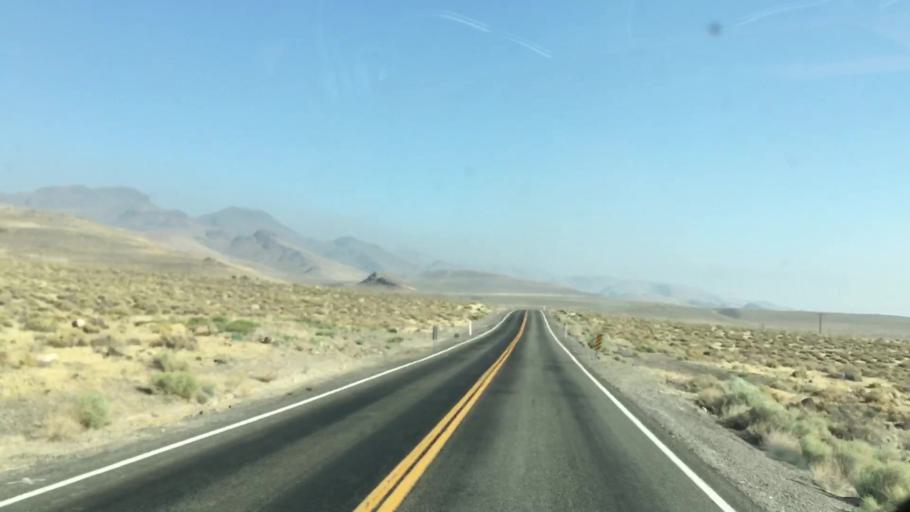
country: US
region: Nevada
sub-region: Lyon County
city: Fernley
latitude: 39.9914
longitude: -119.3857
